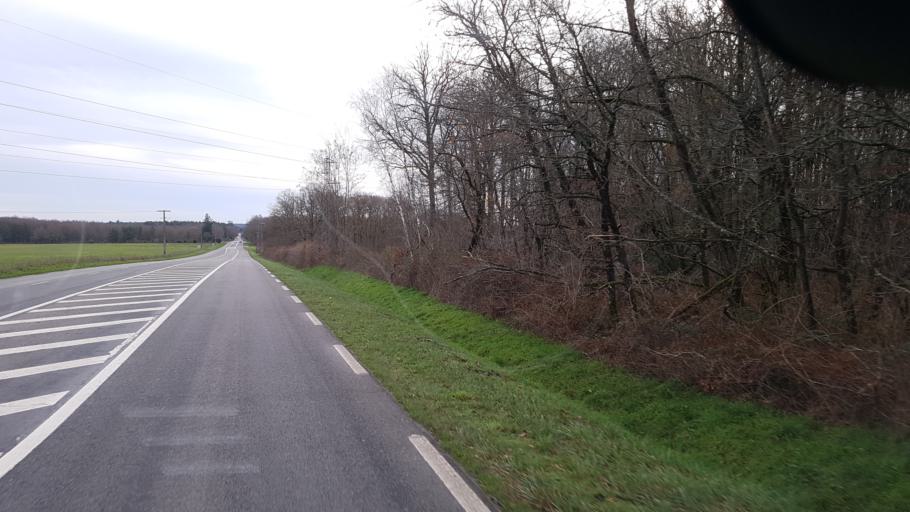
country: FR
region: Centre
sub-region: Departement du Loir-et-Cher
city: Nouan-le-Fuzelier
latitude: 47.5594
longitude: 2.0321
